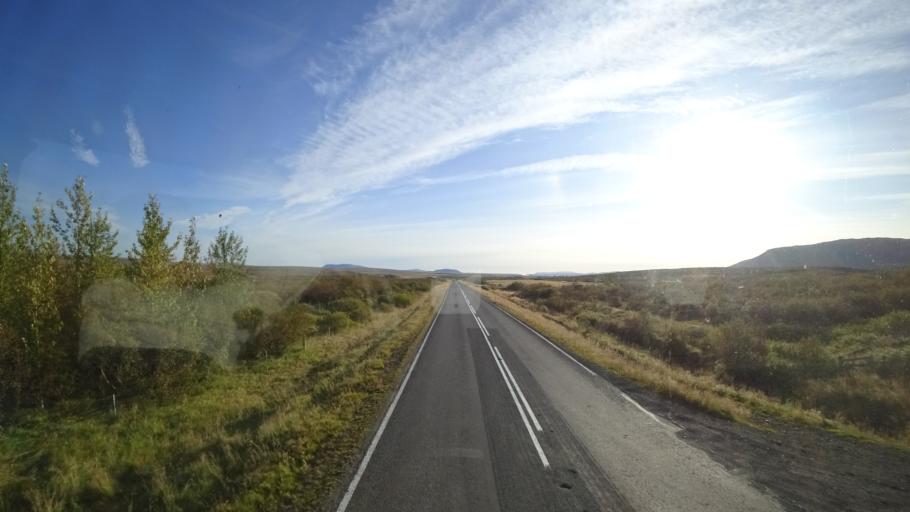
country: IS
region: South
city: Selfoss
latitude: 64.2642
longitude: -20.4684
